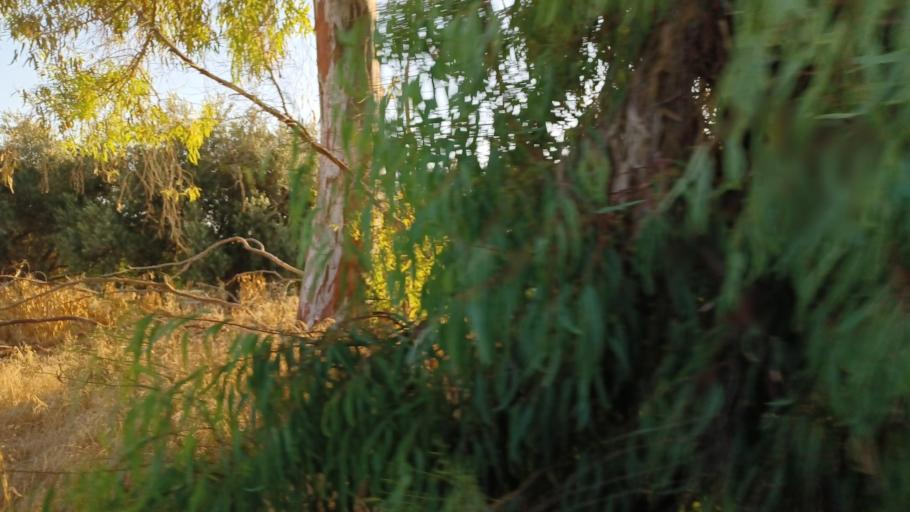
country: CY
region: Pafos
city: Polis
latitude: 35.0588
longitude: 32.4594
